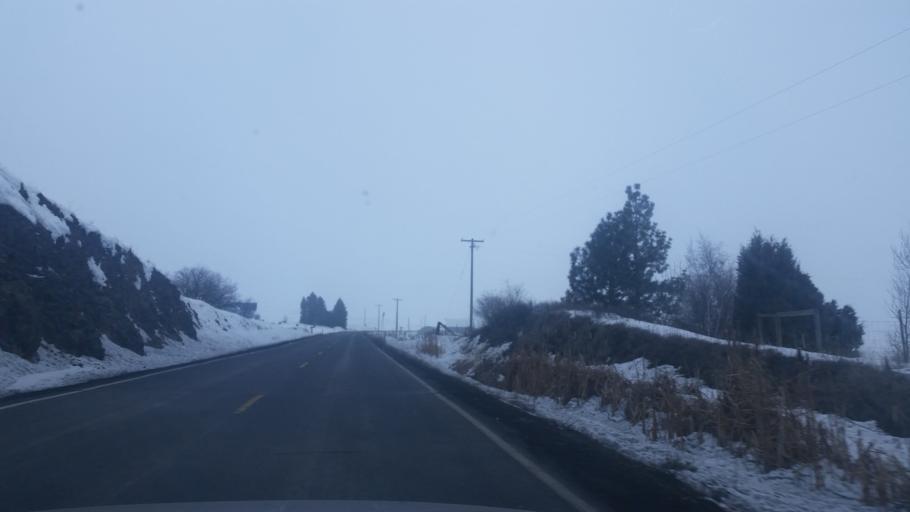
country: US
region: Washington
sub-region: Spokane County
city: Medical Lake
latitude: 47.7166
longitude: -117.8716
